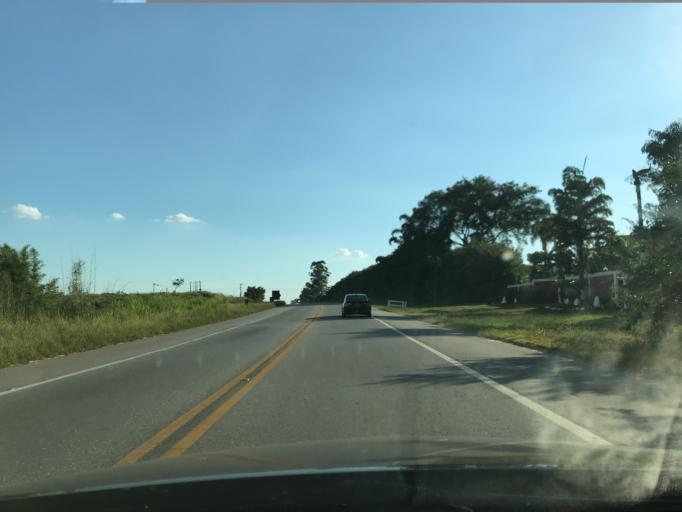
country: BR
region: Sao Paulo
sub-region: Tremembe
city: Tremembe
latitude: -22.9661
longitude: -45.6404
